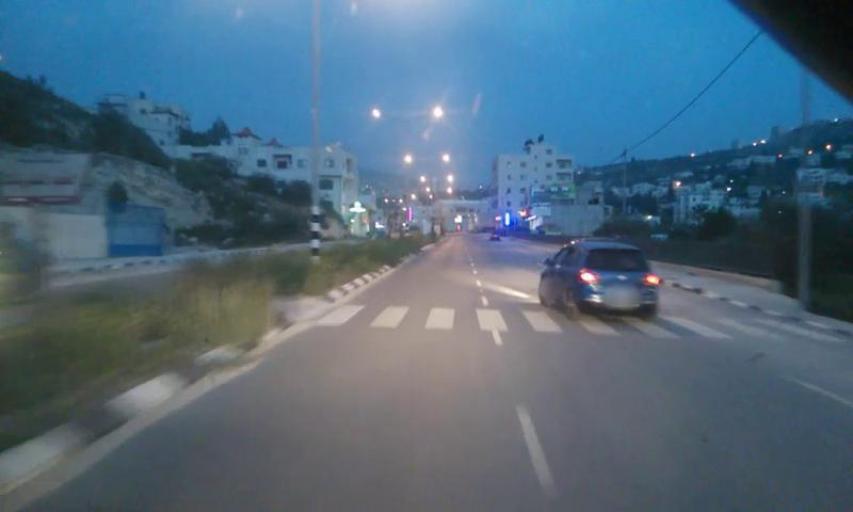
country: PS
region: West Bank
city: Bayt Iba
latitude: 32.2415
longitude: 35.2070
